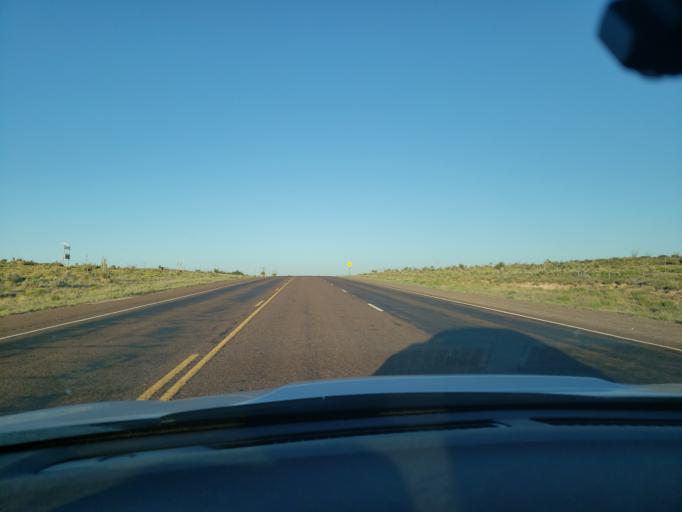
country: US
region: Texas
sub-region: El Paso County
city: Homestead Meadows South
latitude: 31.8271
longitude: -105.8872
